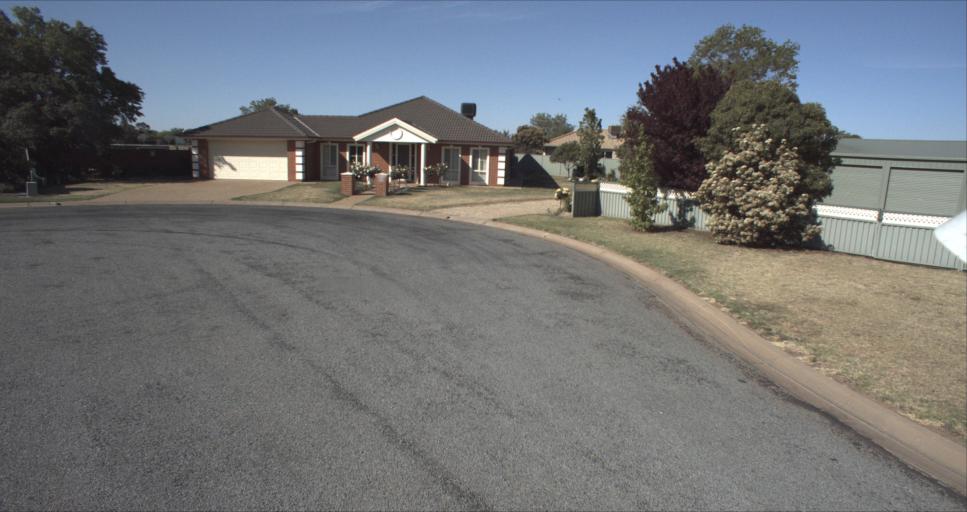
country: AU
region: New South Wales
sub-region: Leeton
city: Leeton
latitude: -34.5544
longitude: 146.4136
